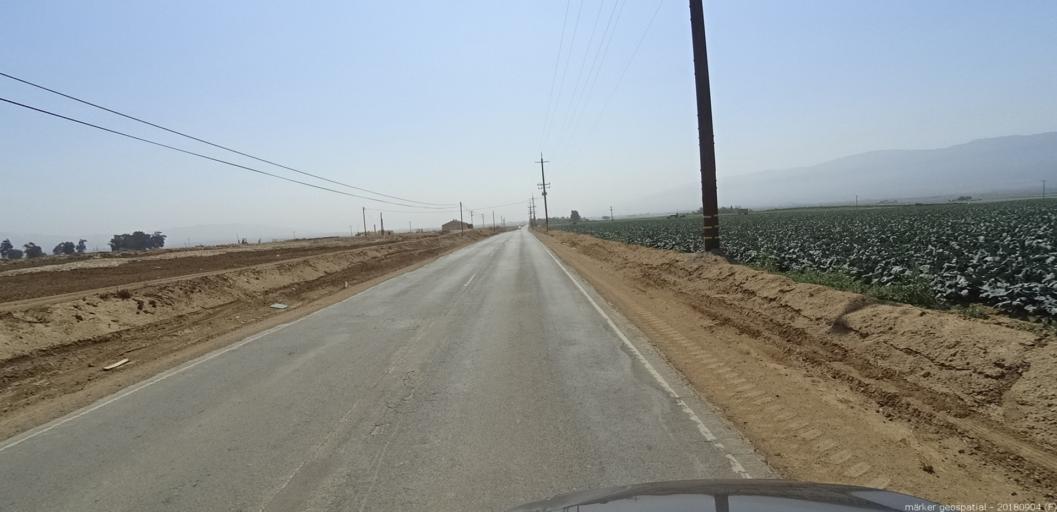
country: US
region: California
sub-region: Monterey County
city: Chualar
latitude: 36.5593
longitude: -121.4803
